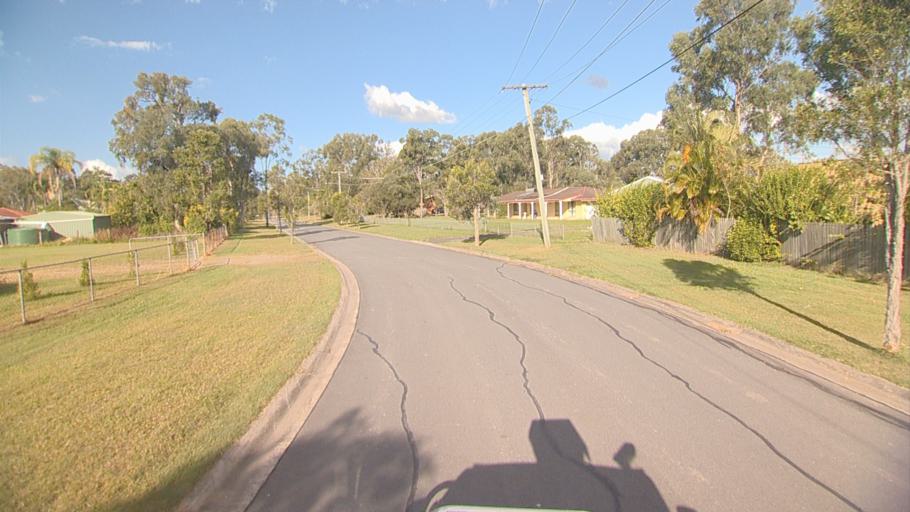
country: AU
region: Queensland
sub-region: Logan
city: Beenleigh
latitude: -27.6705
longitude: 153.2051
